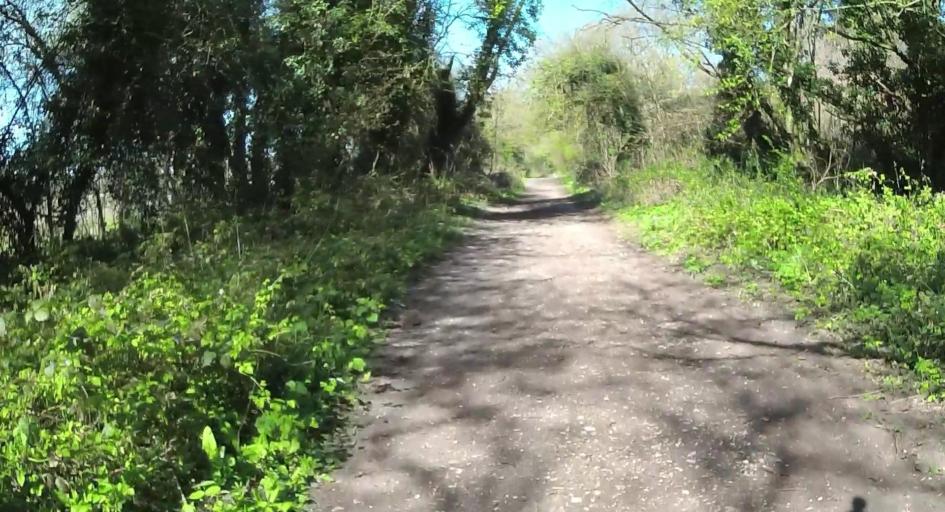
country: GB
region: England
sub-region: Hampshire
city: Romsey
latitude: 51.0908
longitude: -1.4992
